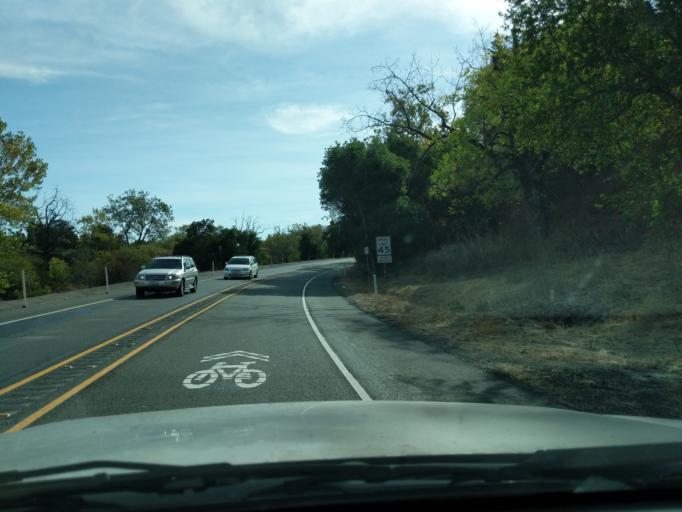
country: US
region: California
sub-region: Alameda County
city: Fremont
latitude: 37.5828
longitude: -121.9645
